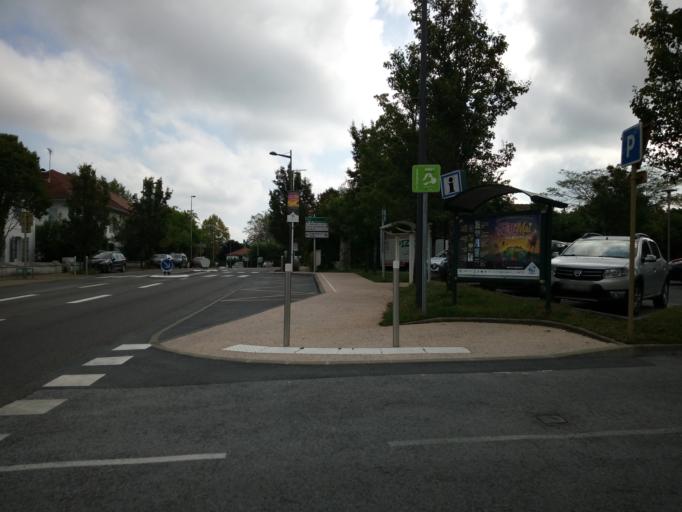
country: FR
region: Aquitaine
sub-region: Departement des Landes
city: Saint-Martin-de-Seignanx
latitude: 43.5293
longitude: -1.3886
